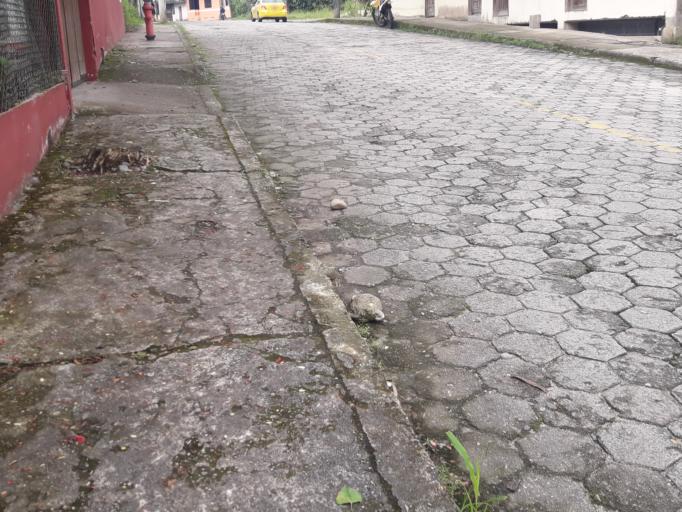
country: EC
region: Napo
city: Tena
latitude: -0.9953
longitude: -77.8144
